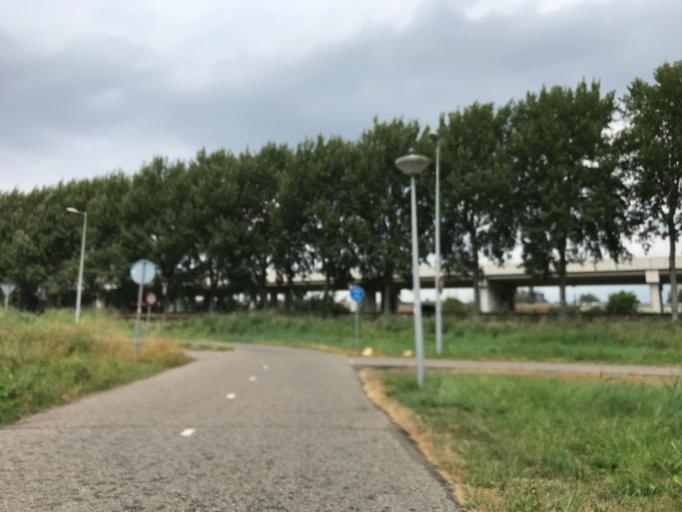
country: NL
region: North Holland
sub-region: Gemeente Ouder-Amstel
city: Duivendrecht
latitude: 52.3269
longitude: 4.9081
